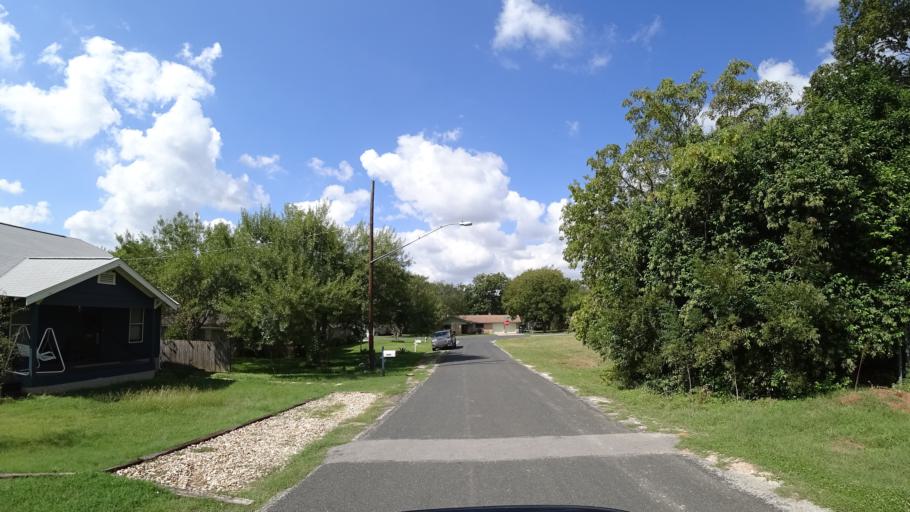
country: US
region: Texas
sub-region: Travis County
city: Onion Creek
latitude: 30.1936
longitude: -97.7958
